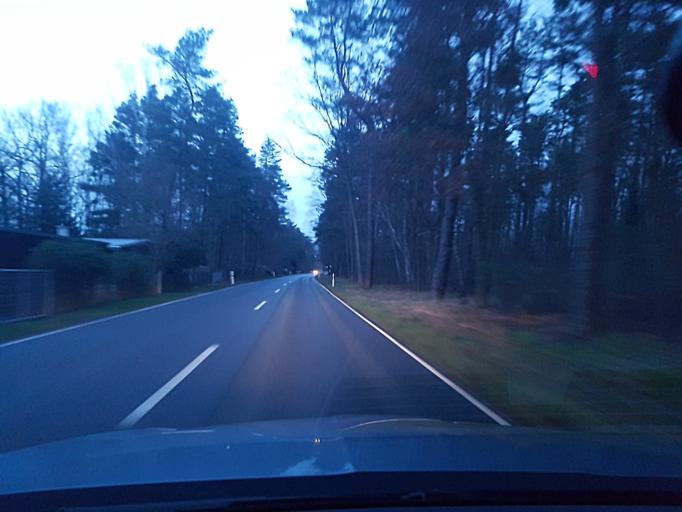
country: DE
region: Brandenburg
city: Ruckersdorf
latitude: 51.5898
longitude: 13.5605
